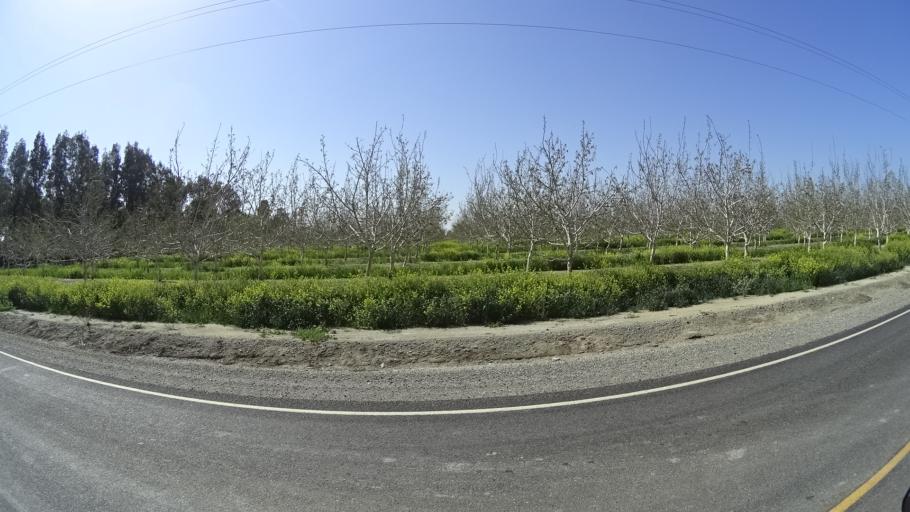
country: US
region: California
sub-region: Glenn County
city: Hamilton City
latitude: 39.6597
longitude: -122.0574
